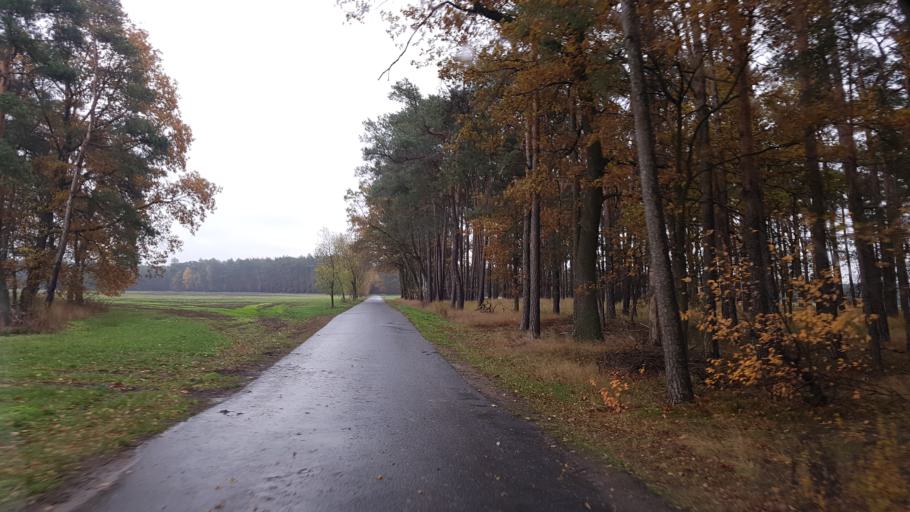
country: DE
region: Brandenburg
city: Herzberg
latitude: 51.6587
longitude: 13.2378
